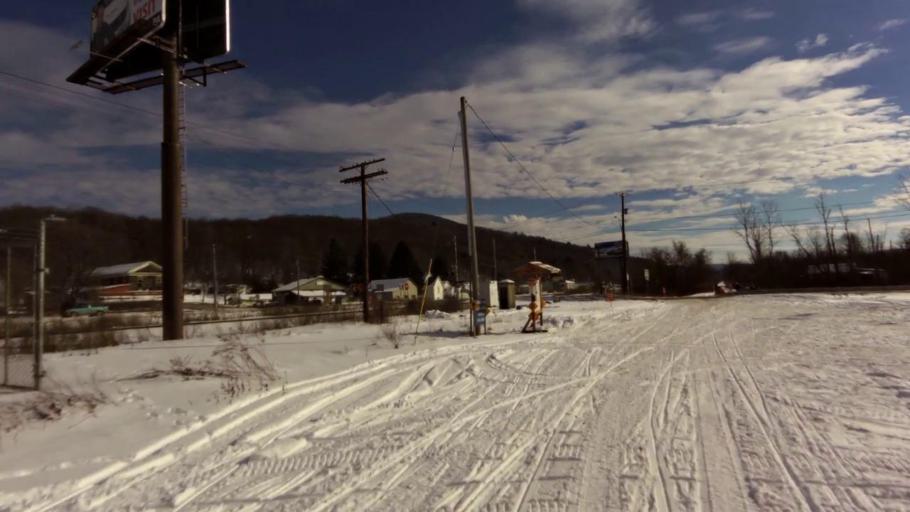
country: US
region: Pennsylvania
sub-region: McKean County
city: Foster Brook
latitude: 42.0237
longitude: -78.6305
